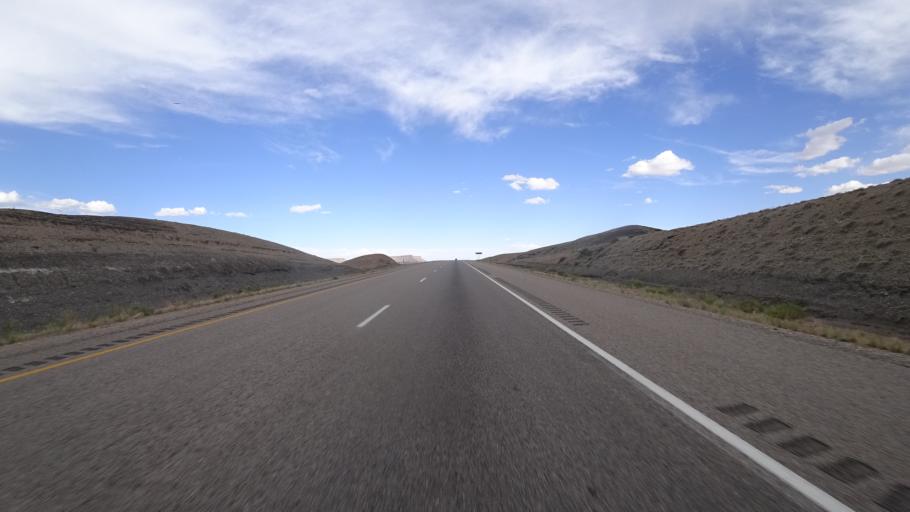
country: US
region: Utah
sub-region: Carbon County
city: East Carbon City
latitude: 38.9690
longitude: -110.0928
